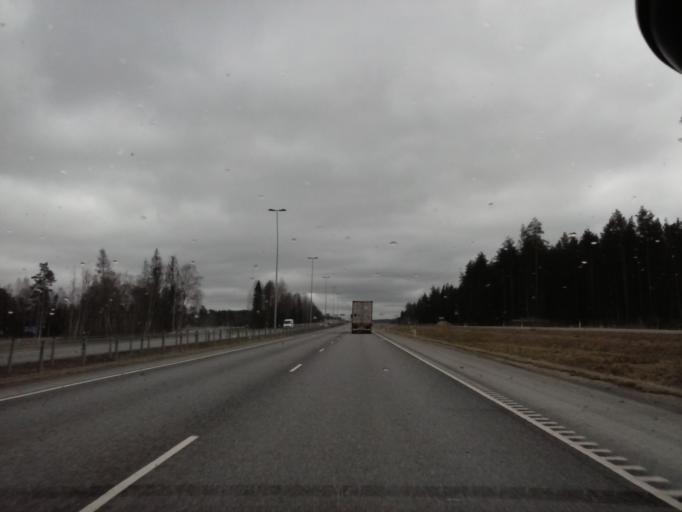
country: EE
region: Harju
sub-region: Rae vald
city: Vaida
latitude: 59.2273
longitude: 25.0325
